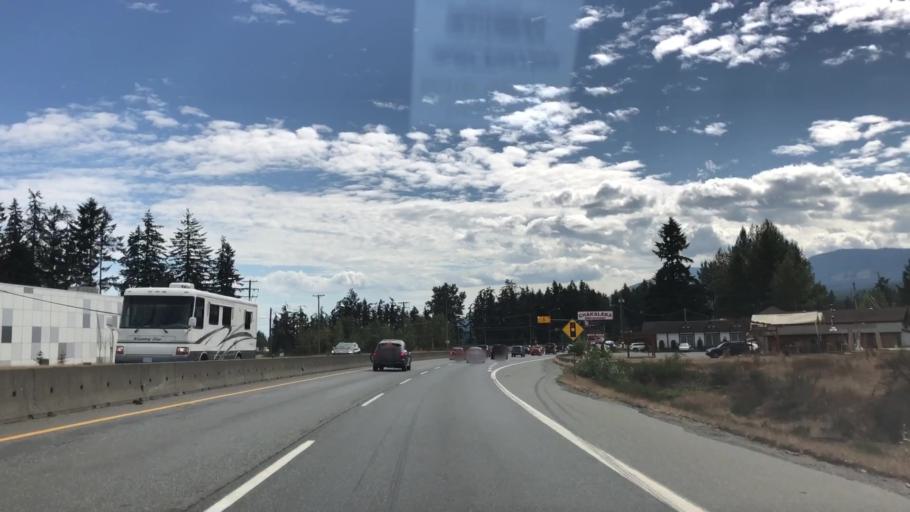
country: CA
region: British Columbia
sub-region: Cowichan Valley Regional District
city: Ladysmith
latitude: 49.0374
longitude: -123.8643
